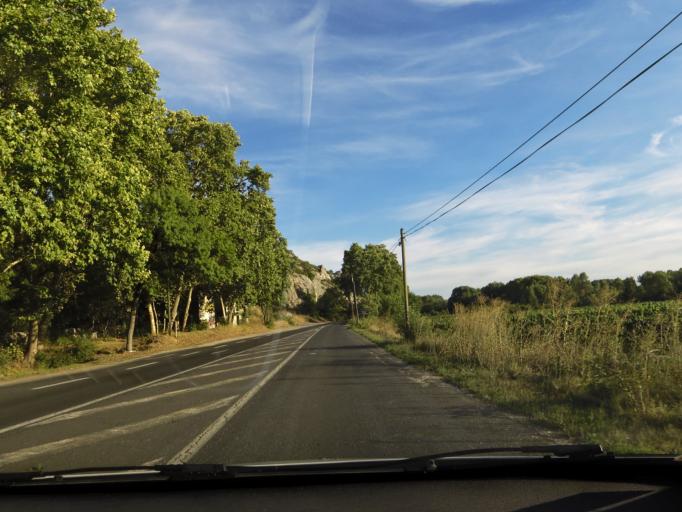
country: FR
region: Languedoc-Roussillon
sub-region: Departement de l'Herault
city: Prades-le-Lez
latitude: 43.7092
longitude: 3.8676
